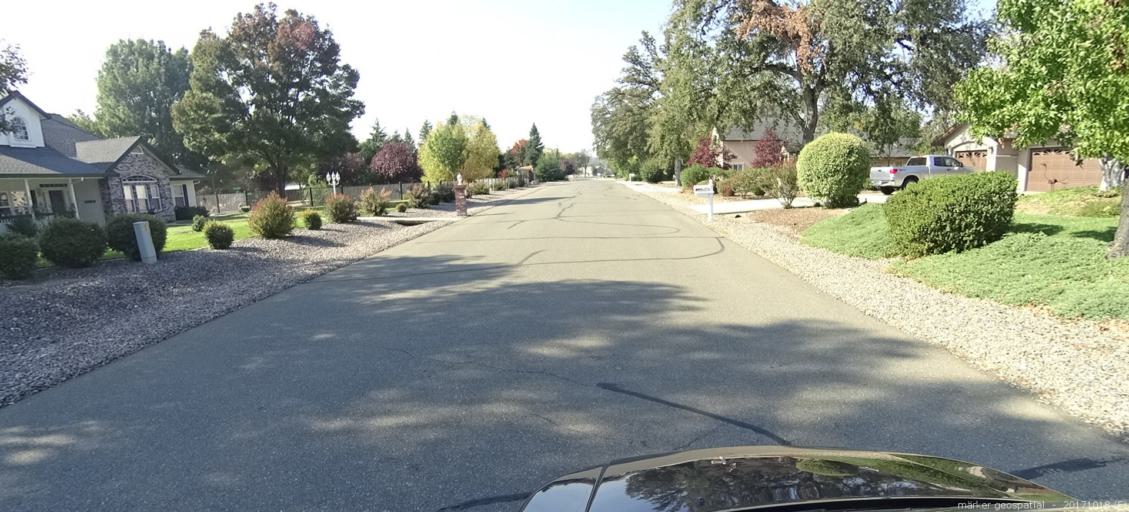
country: US
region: California
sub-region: Shasta County
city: Palo Cedro
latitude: 40.5586
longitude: -122.2332
